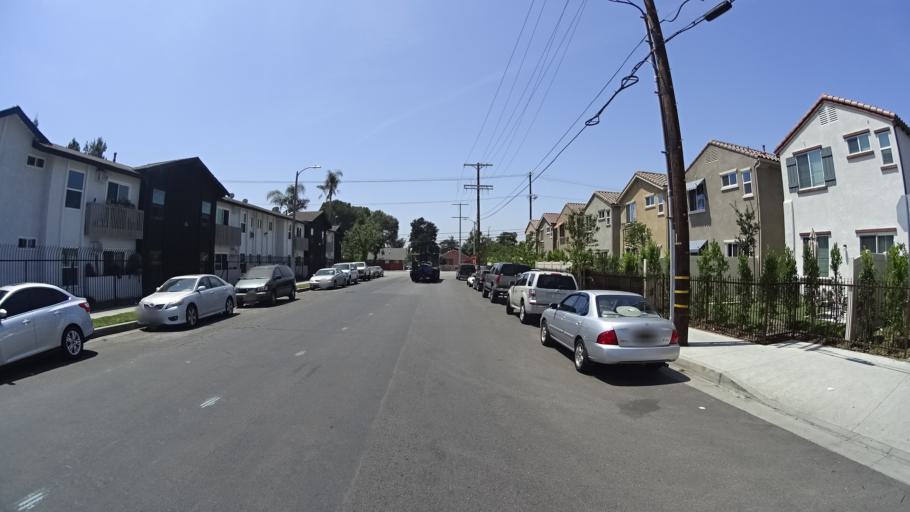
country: US
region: California
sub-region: Los Angeles County
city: Van Nuys
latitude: 34.2092
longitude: -118.4630
